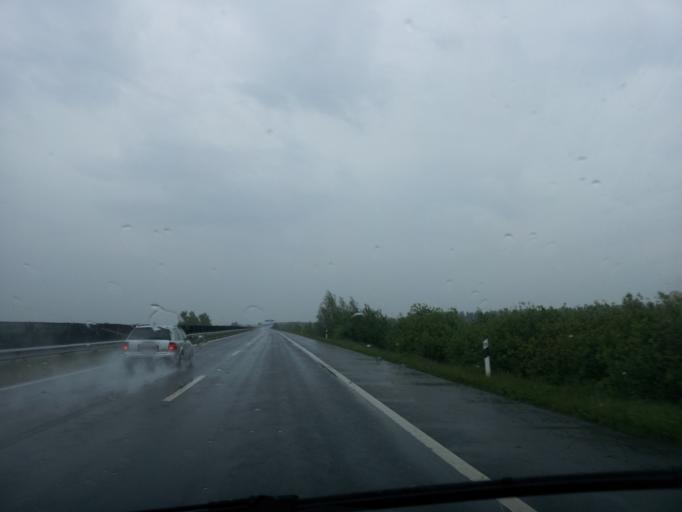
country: HU
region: Tolna
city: Ocseny
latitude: 46.3557
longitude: 18.7558
